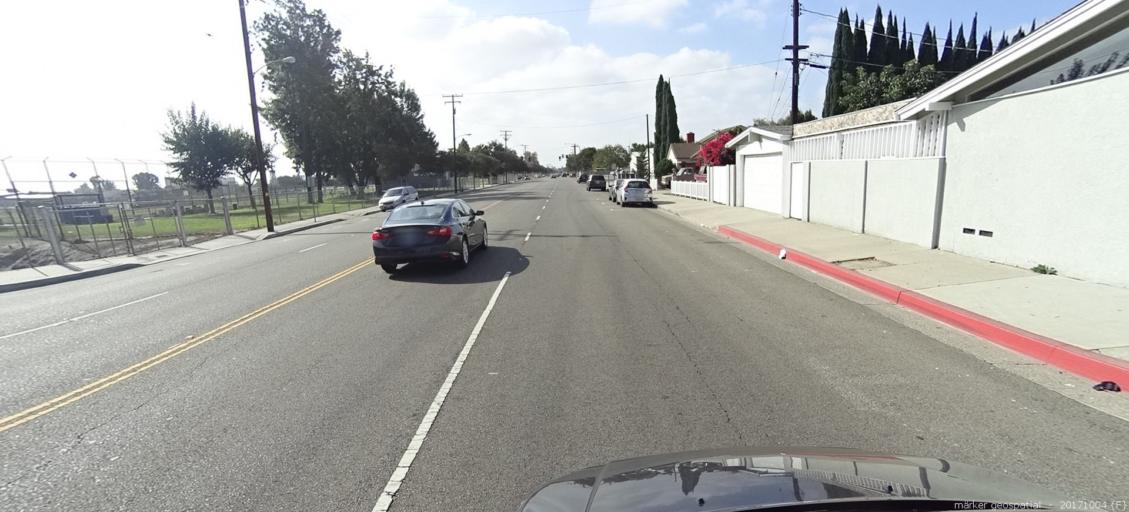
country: US
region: California
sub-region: Orange County
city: Garden Grove
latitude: 33.7874
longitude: -117.9237
